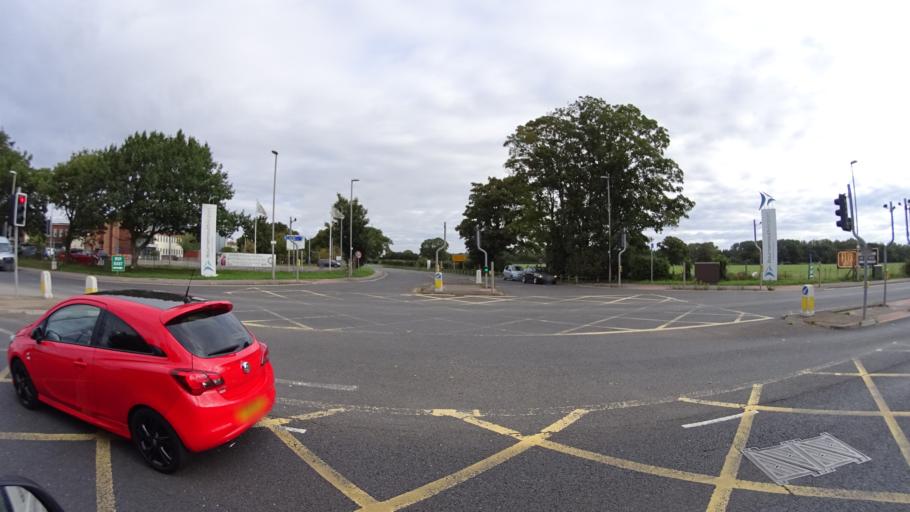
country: GB
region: England
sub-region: Dorset
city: St Leonards
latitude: 50.7743
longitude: -1.8322
